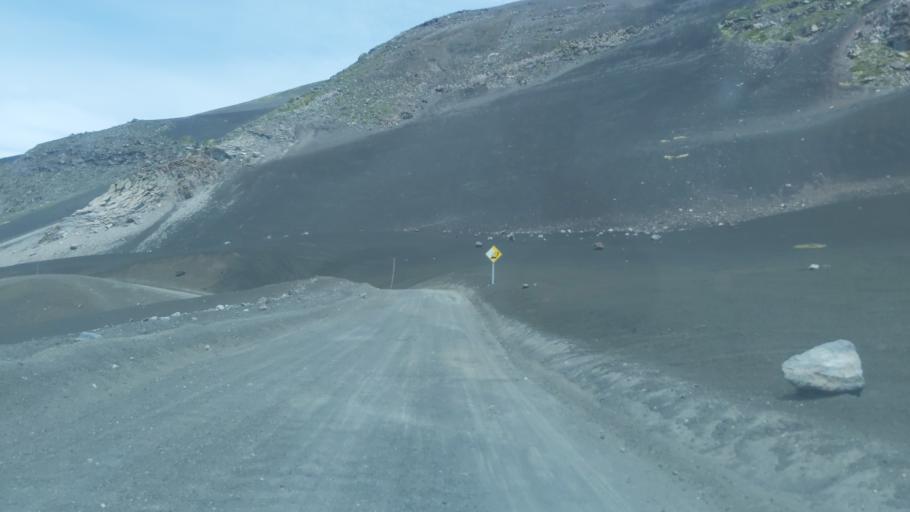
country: AR
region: Neuquen
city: Andacollo
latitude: -37.4033
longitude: -71.3021
